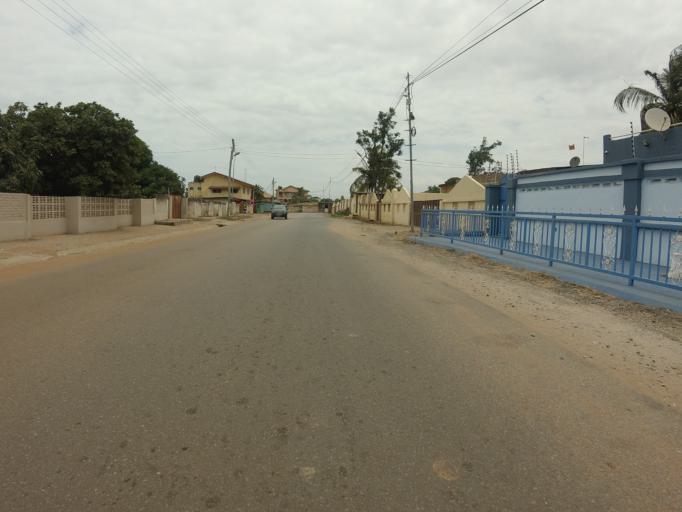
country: GH
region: Greater Accra
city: Teshi Old Town
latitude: 5.6050
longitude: -0.1031
